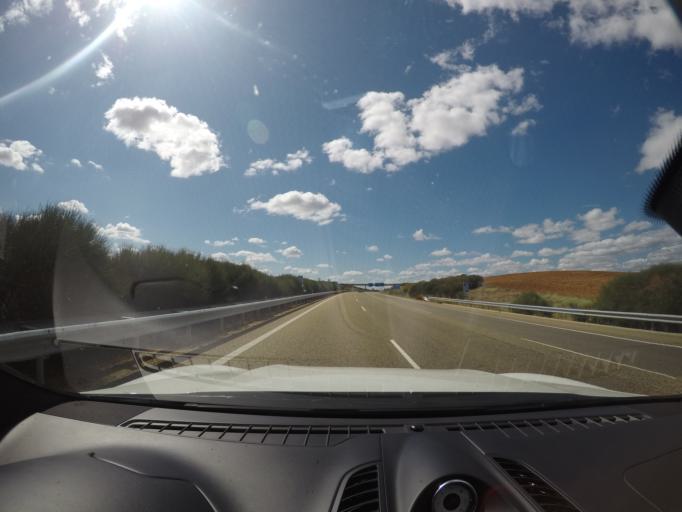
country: ES
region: Castille and Leon
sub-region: Provincia de Zamora
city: San Cristobal de Entrevinas
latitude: 42.0633
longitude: -5.6686
